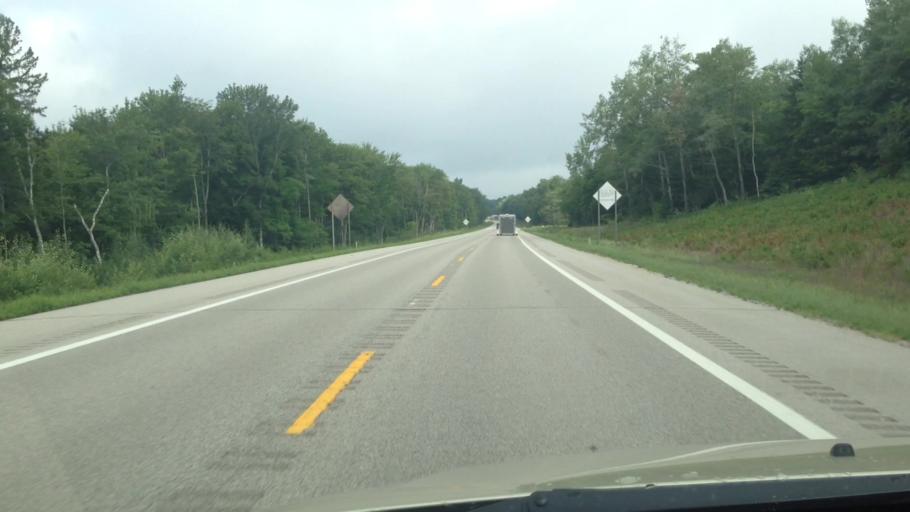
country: US
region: Michigan
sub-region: Luce County
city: Newberry
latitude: 46.0576
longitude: -85.1631
